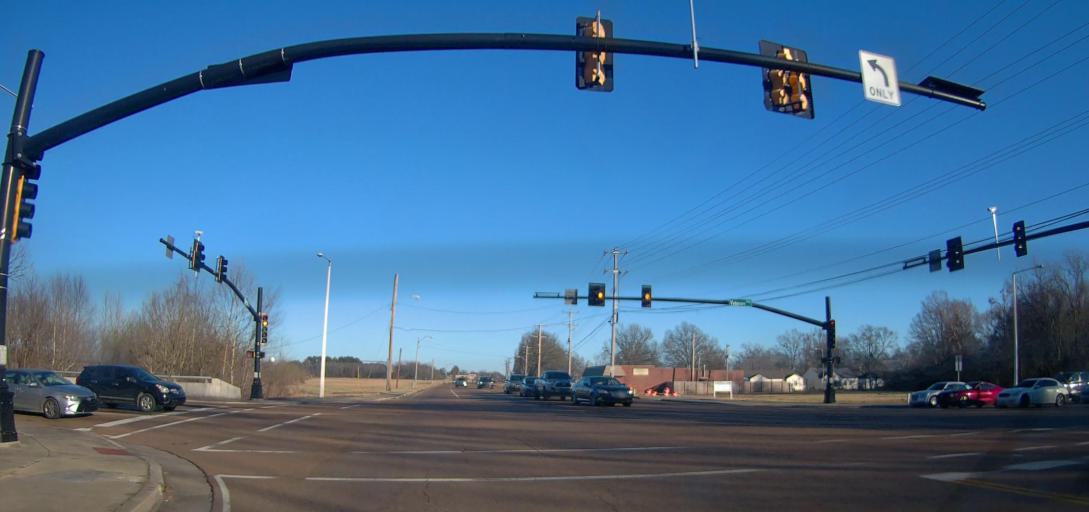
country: US
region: Tennessee
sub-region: Shelby County
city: Millington
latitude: 35.3414
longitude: -89.8889
